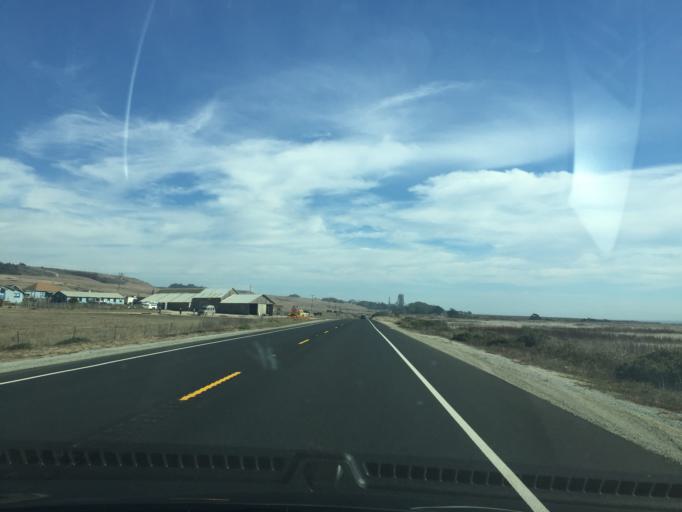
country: US
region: California
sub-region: Santa Cruz County
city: Bonny Doon
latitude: 37.0312
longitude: -122.2205
